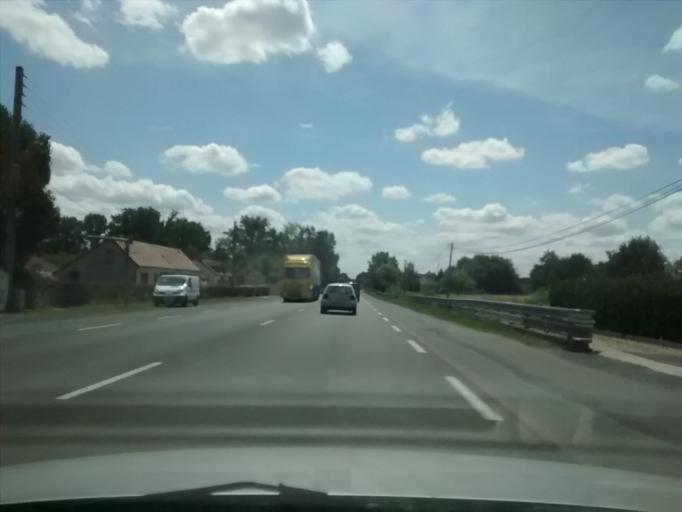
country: FR
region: Pays de la Loire
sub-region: Departement de la Sarthe
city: Ruaudin
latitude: 47.9478
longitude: 0.2319
